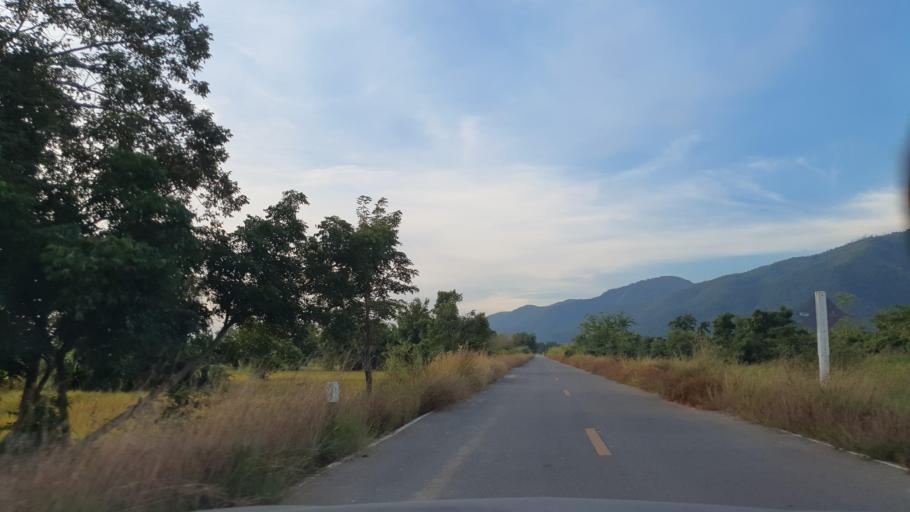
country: TH
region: Uthai Thani
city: Sawang Arom
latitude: 15.7039
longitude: 99.9615
